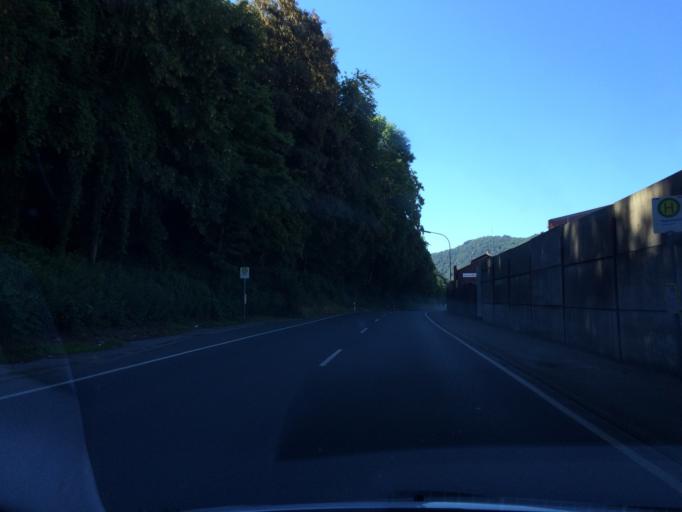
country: DE
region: North Rhine-Westphalia
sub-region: Regierungsbezirk Arnsberg
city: Nachrodt-Wiblingwerde
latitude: 51.3512
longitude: 7.6417
